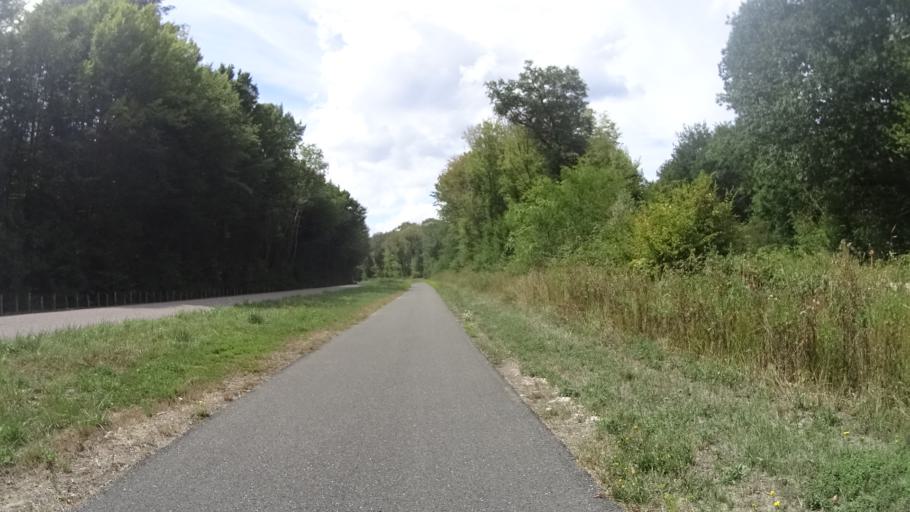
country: FR
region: Franche-Comte
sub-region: Departement du Jura
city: Damparis
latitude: 47.0748
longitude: 5.3762
